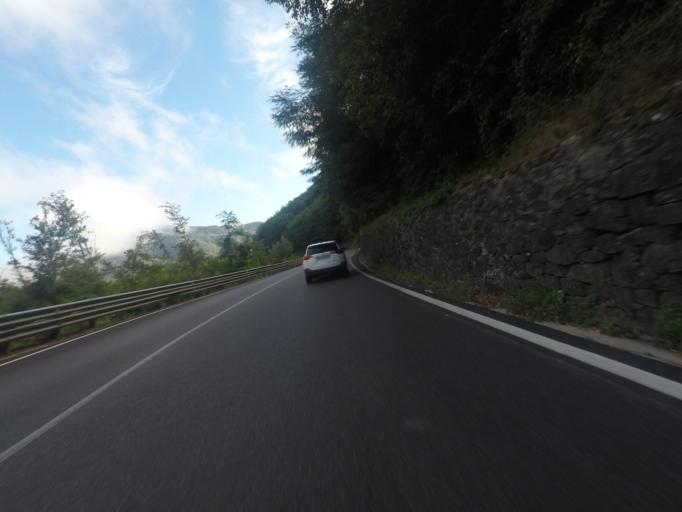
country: IT
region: Tuscany
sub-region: Provincia di Lucca
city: Bagni di Lucca
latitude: 43.9946
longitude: 10.5553
